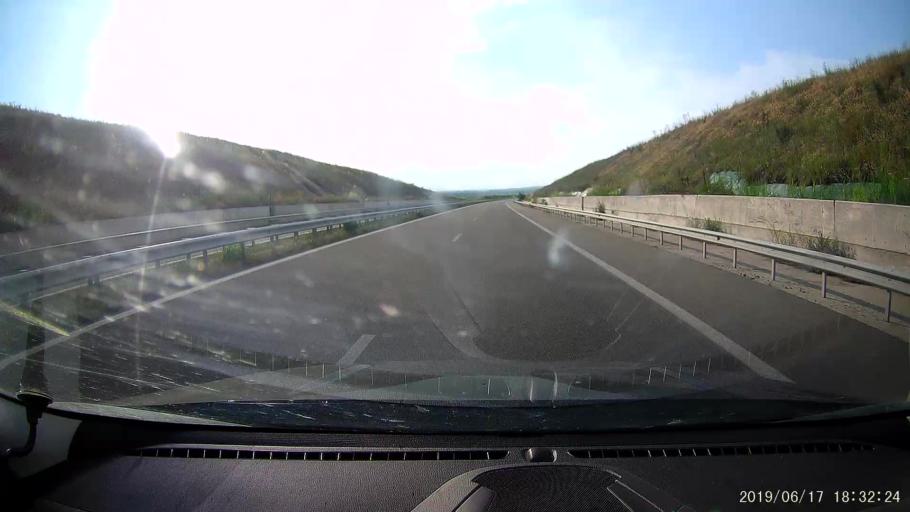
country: BG
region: Khaskovo
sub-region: Obshtina Dimitrovgrad
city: Dimitrovgrad
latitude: 42.0592
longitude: 25.4797
